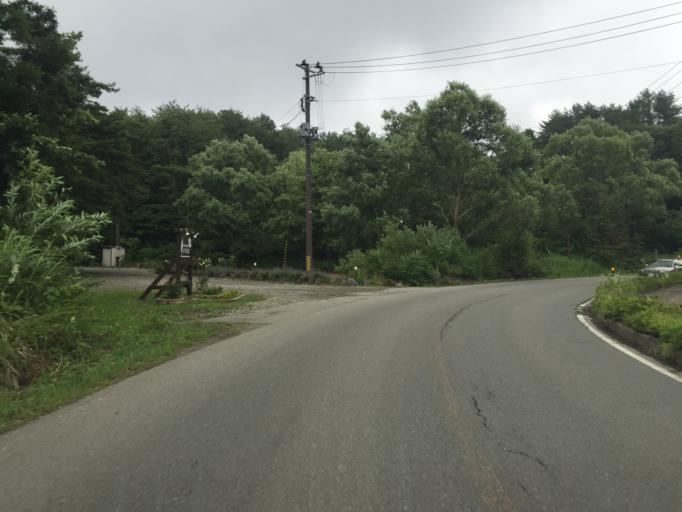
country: JP
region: Fukushima
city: Inawashiro
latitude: 37.6712
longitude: 140.0777
